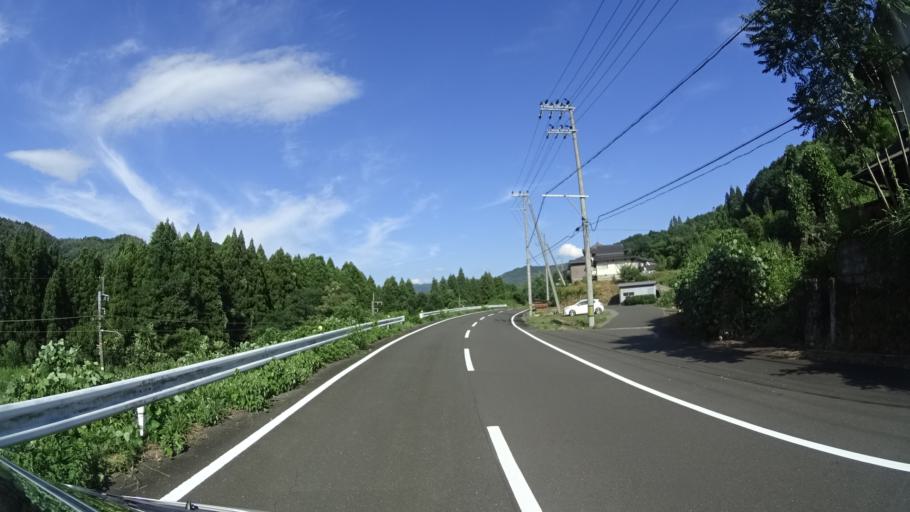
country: JP
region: Kyoto
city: Ayabe
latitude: 35.2872
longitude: 135.2826
